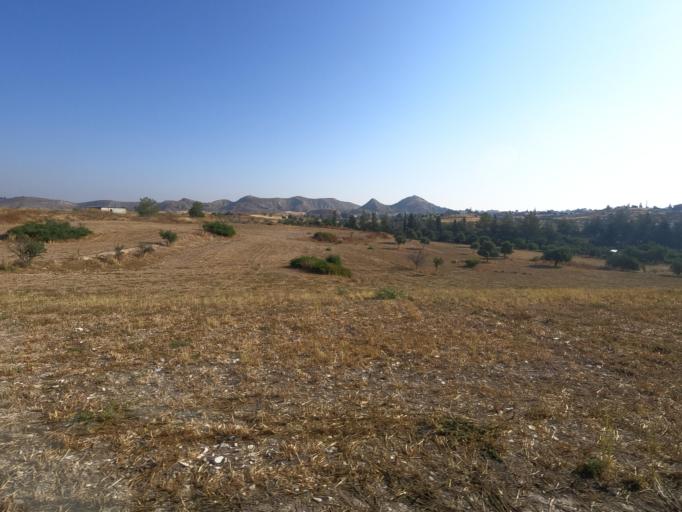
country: CY
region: Lefkosia
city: Lympia
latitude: 34.9911
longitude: 33.4517
